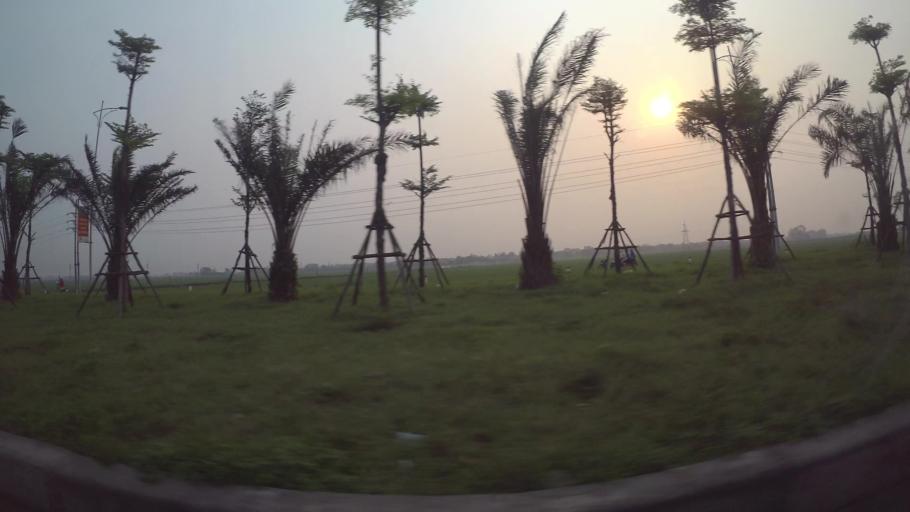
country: VN
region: Ha Noi
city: Kim Bai
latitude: 20.8871
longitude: 105.7966
